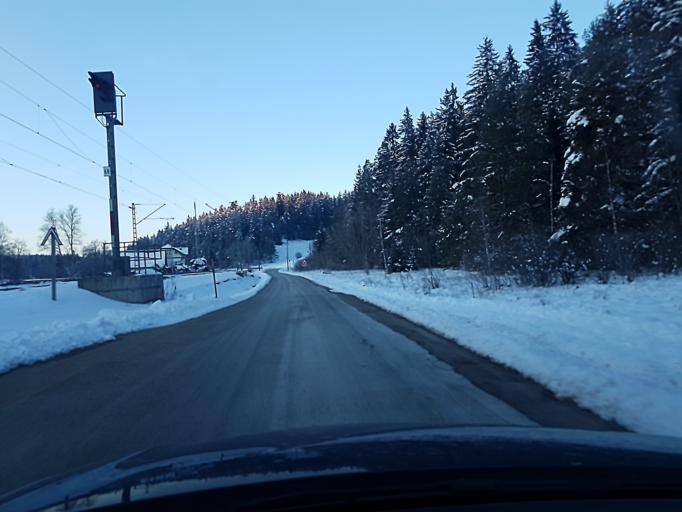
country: DE
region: Baden-Wuerttemberg
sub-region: Freiburg Region
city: Monchweiler
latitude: 48.0880
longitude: 8.4049
